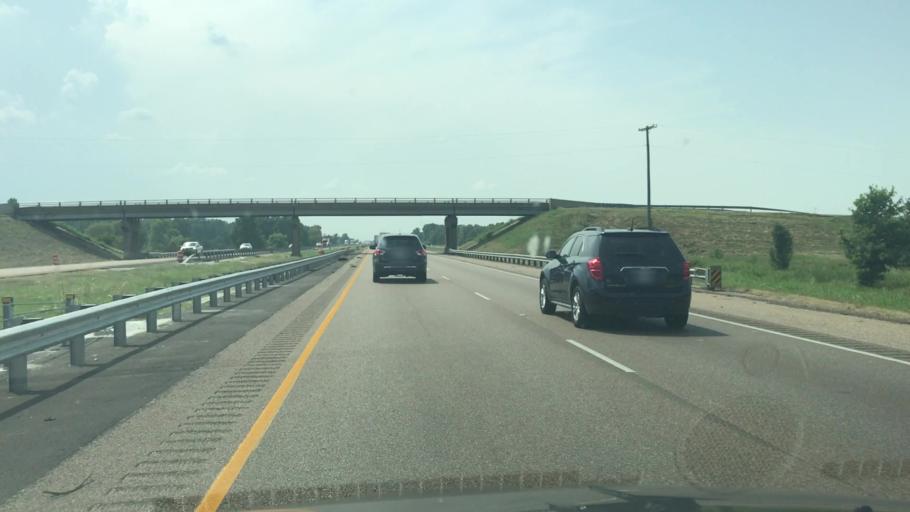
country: US
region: Arkansas
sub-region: Crittenden County
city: Earle
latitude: 35.1499
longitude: -90.3626
